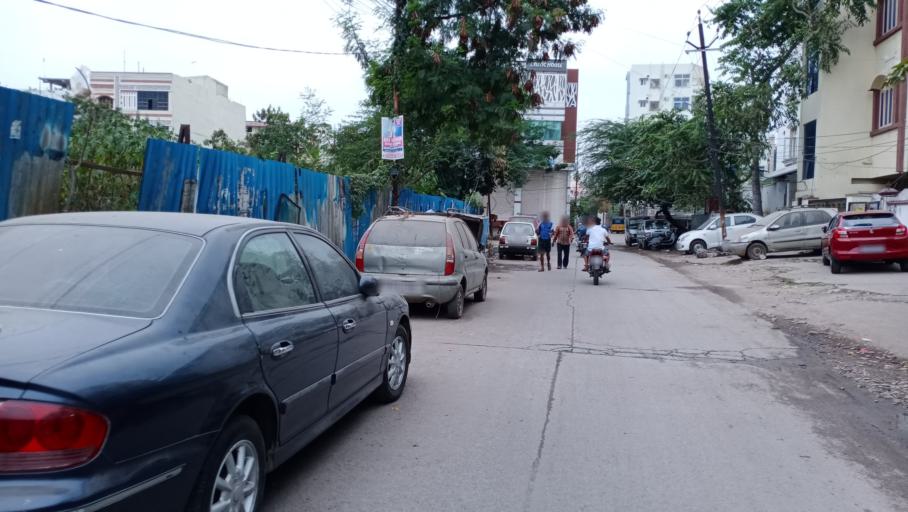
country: IN
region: Telangana
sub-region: Hyderabad
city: Hyderabad
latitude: 17.4098
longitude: 78.4360
